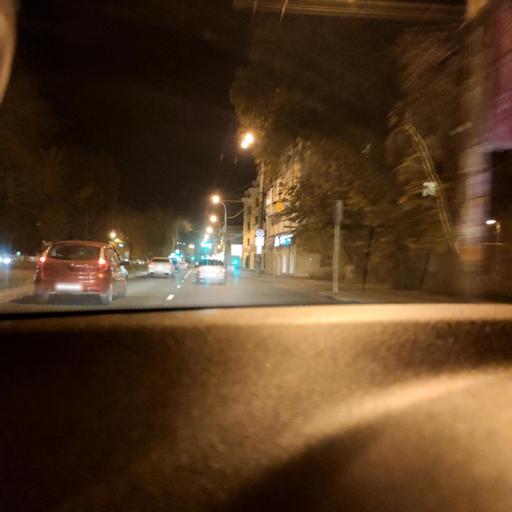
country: RU
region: Samara
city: Samara
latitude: 53.2173
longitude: 50.2588
